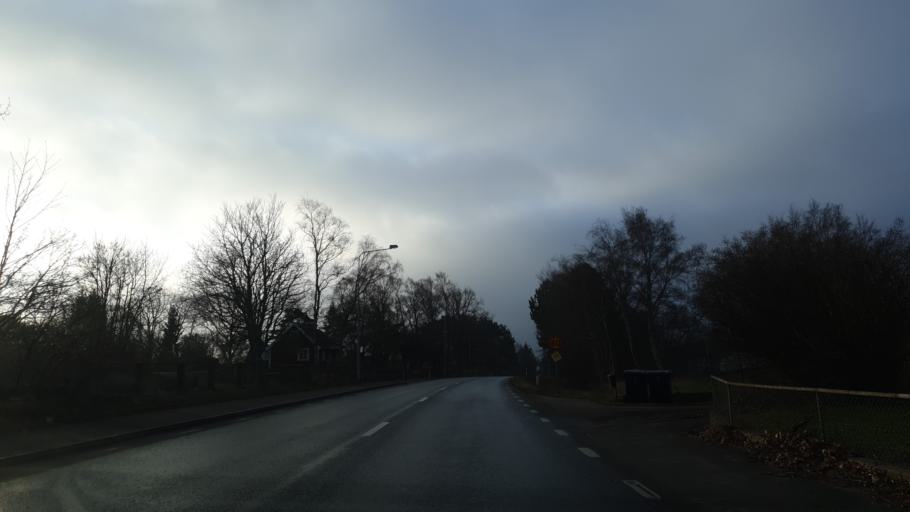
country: SE
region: Blekinge
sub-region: Karlshamns Kommun
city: Morrum
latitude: 56.1593
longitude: 14.6788
